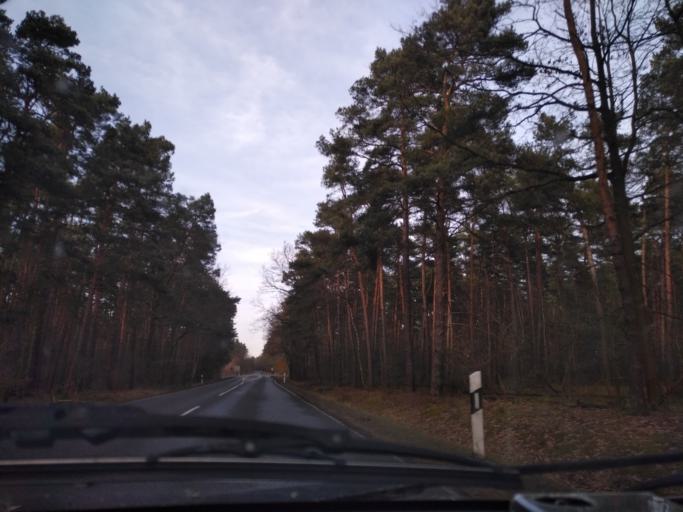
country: DE
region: Saxony-Anhalt
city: Holzdorf
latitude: 51.8451
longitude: 13.1450
